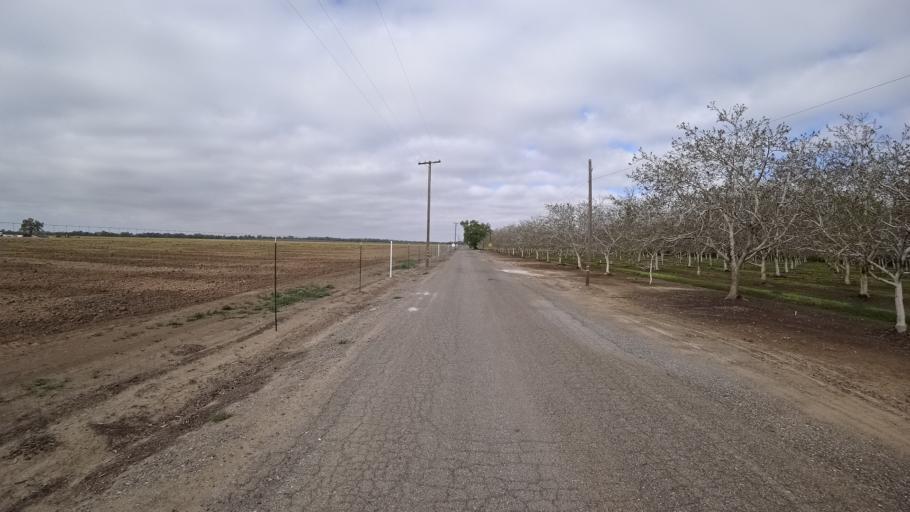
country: US
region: California
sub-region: Colusa County
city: Colusa
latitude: 39.4185
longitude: -121.9675
